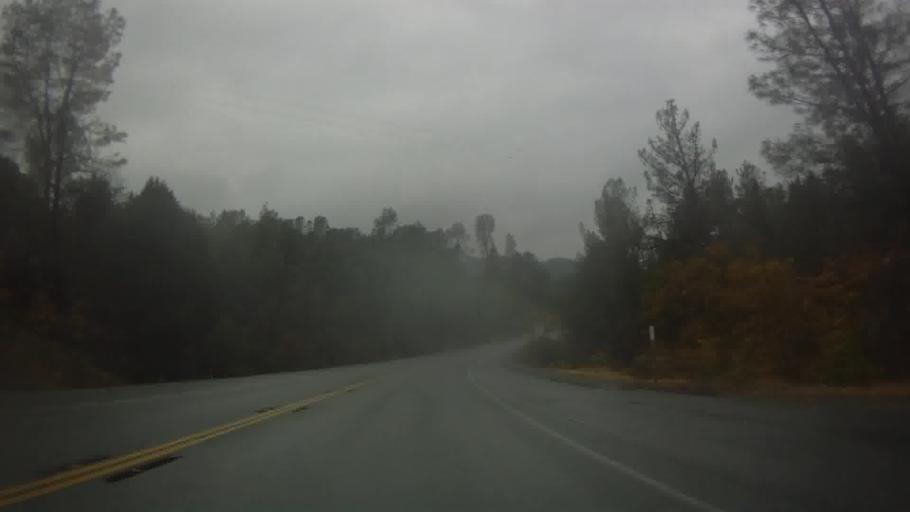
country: US
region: California
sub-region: Shasta County
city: Shasta
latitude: 40.5911
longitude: -122.4817
